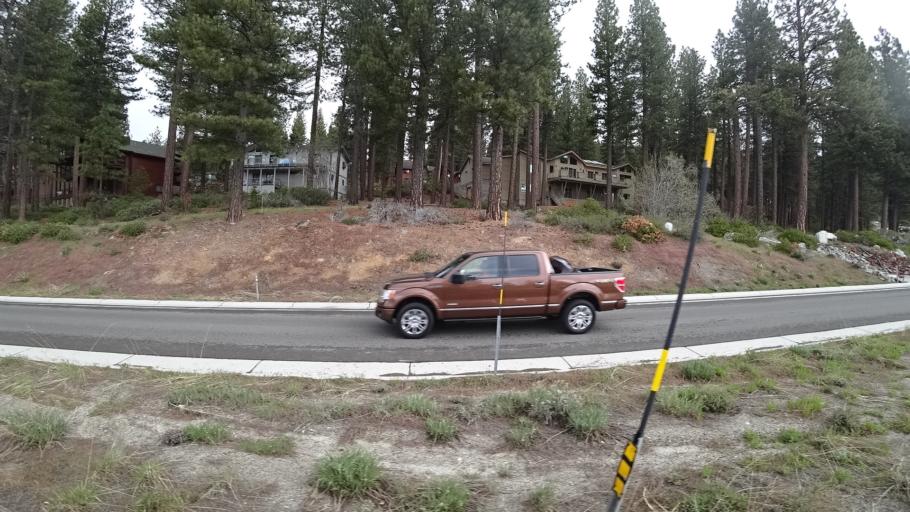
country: US
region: Nevada
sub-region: Washoe County
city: Incline Village
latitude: 39.2514
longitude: -119.9740
